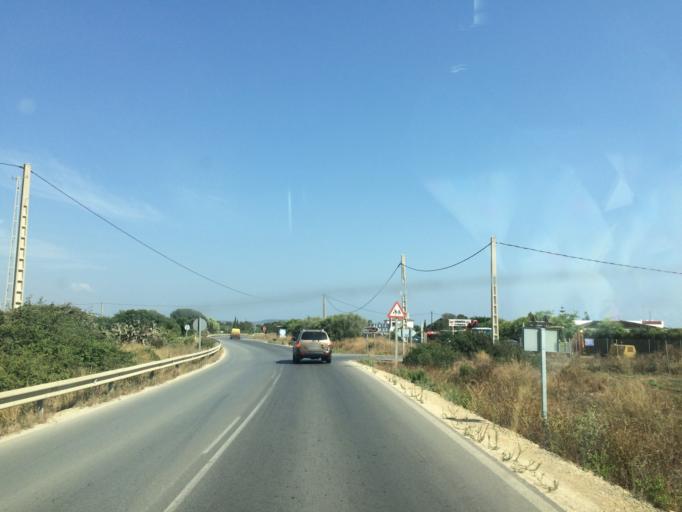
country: ES
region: Andalusia
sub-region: Provincia de Cadiz
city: Conil de la Frontera
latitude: 36.2447
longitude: -6.0635
